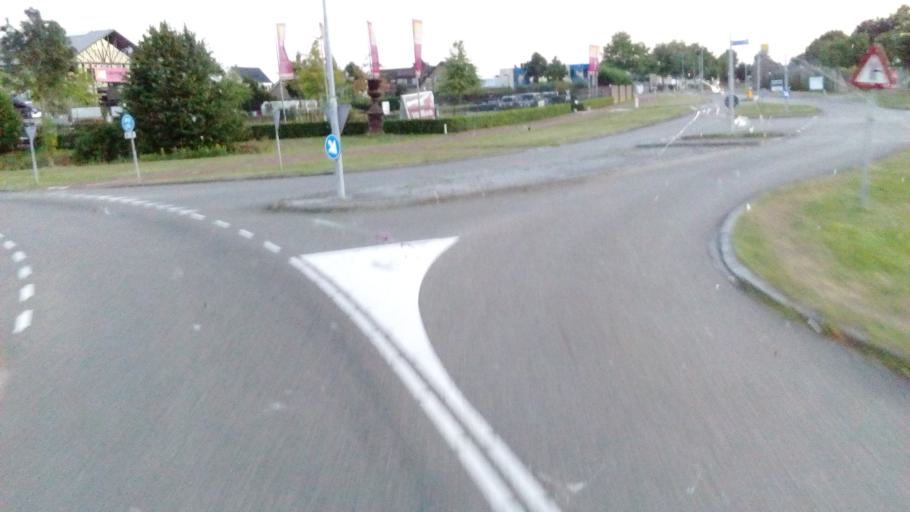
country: NL
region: Gelderland
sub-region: Gemeente Wijchen
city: Wijchen
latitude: 51.8236
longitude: 5.7567
